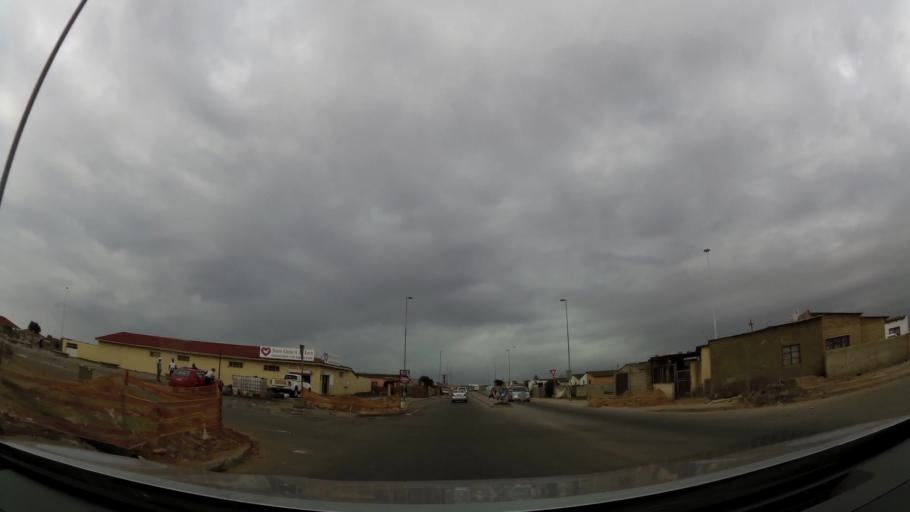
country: ZA
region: Eastern Cape
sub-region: Nelson Mandela Bay Metropolitan Municipality
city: Port Elizabeth
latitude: -33.8922
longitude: 25.5901
